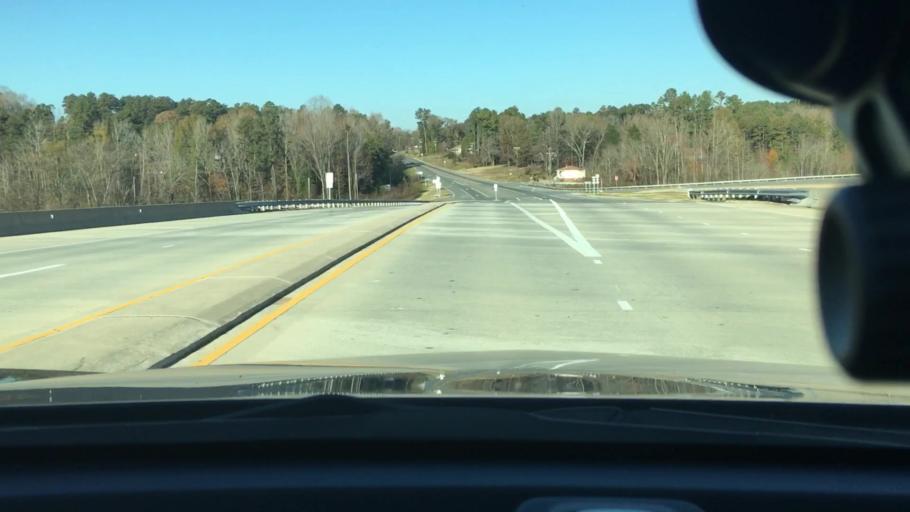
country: US
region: North Carolina
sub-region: Cabarrus County
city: Mount Pleasant
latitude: 35.4068
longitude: -80.4519
